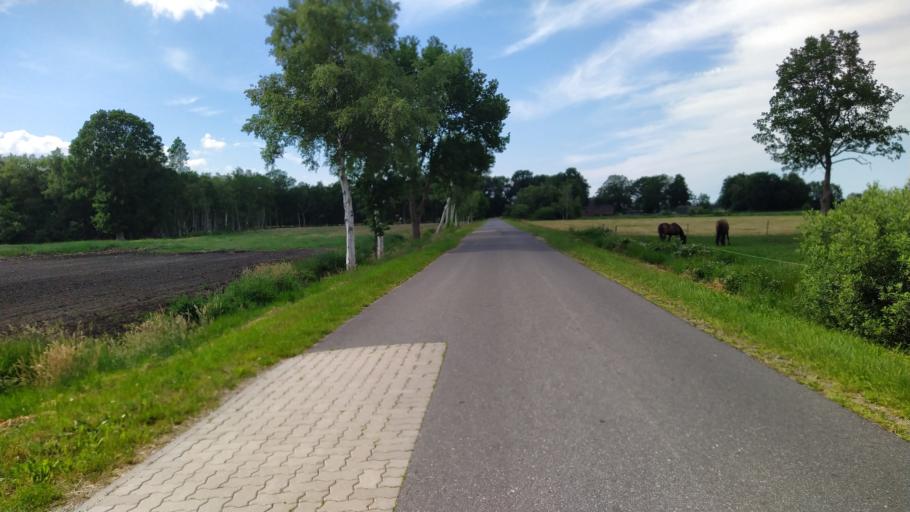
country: DE
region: Lower Saxony
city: Odisheim
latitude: 53.6552
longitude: 8.9356
